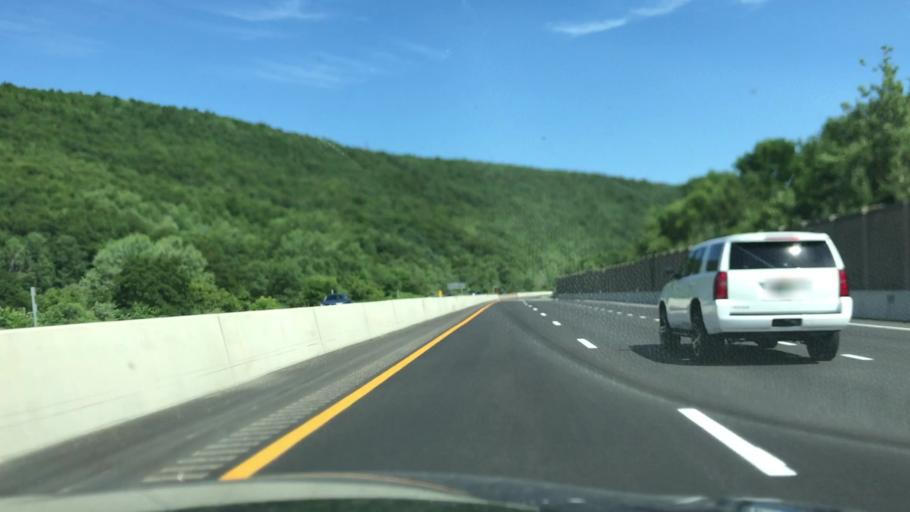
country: US
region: New York
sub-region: Steuben County
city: Corning
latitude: 42.1530
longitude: -77.0475
